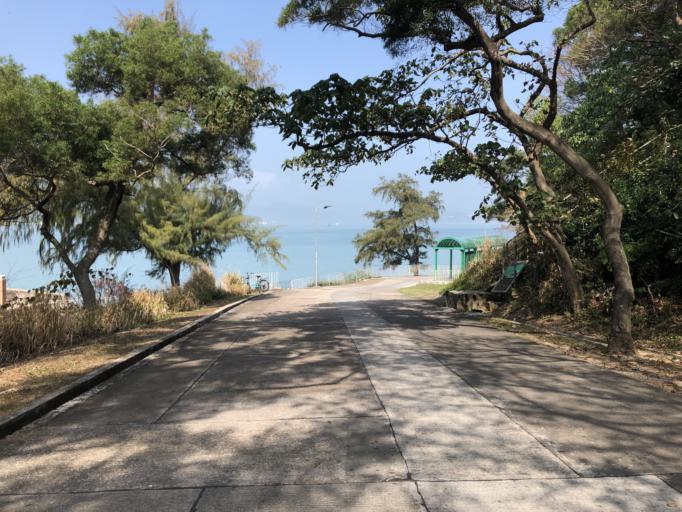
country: HK
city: Yung Shue Wan
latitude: 22.2131
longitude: 114.0242
